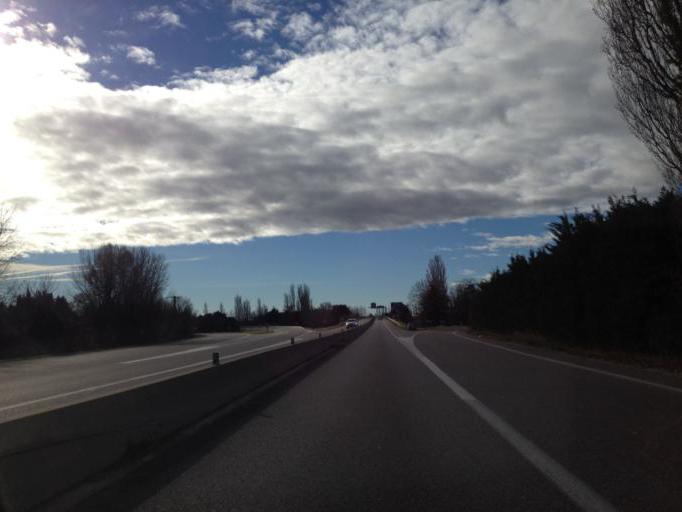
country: FR
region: Provence-Alpes-Cote d'Azur
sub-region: Departement du Vaucluse
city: Orange
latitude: 44.1338
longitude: 4.7939
